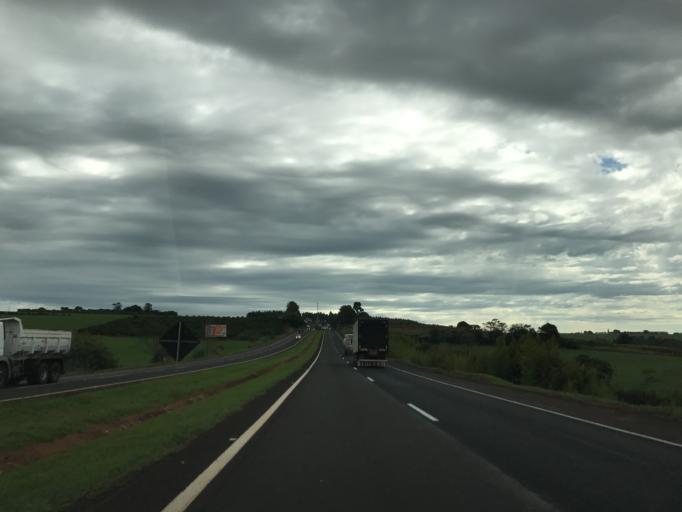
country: BR
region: Parana
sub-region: Rolandia
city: Rolandia
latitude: -23.3105
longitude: -51.3313
